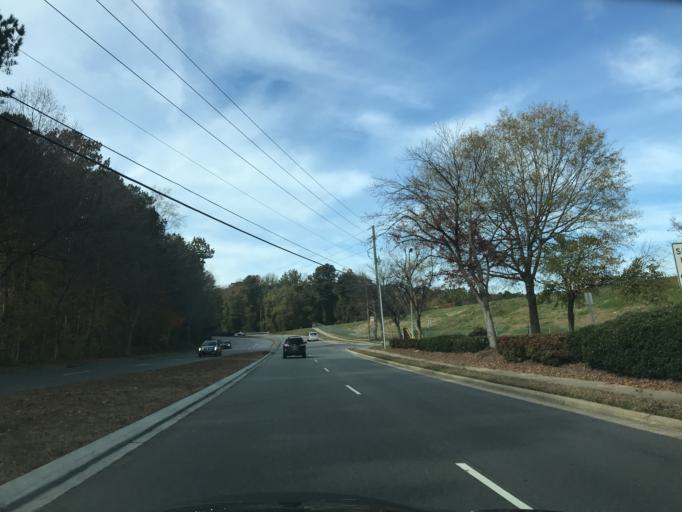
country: US
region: North Carolina
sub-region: Wake County
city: West Raleigh
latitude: 35.8557
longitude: -78.6615
